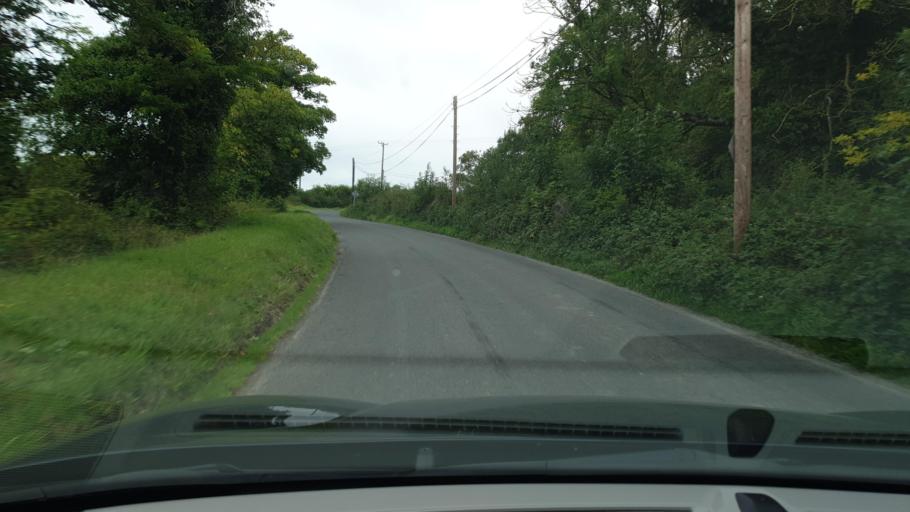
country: IE
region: Leinster
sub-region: An Mhi
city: Ratoath
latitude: 53.5109
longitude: -6.4857
